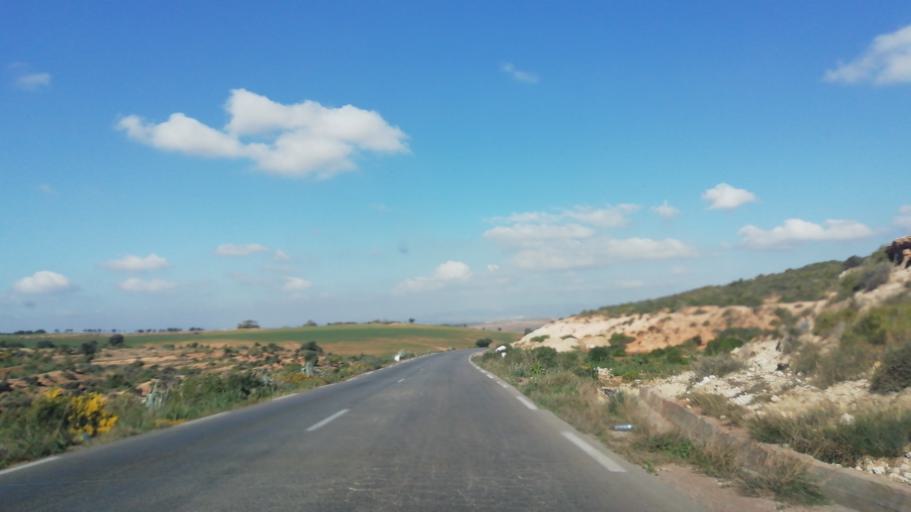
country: DZ
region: Oran
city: Ain el Bya
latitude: 35.7225
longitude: -0.2428
